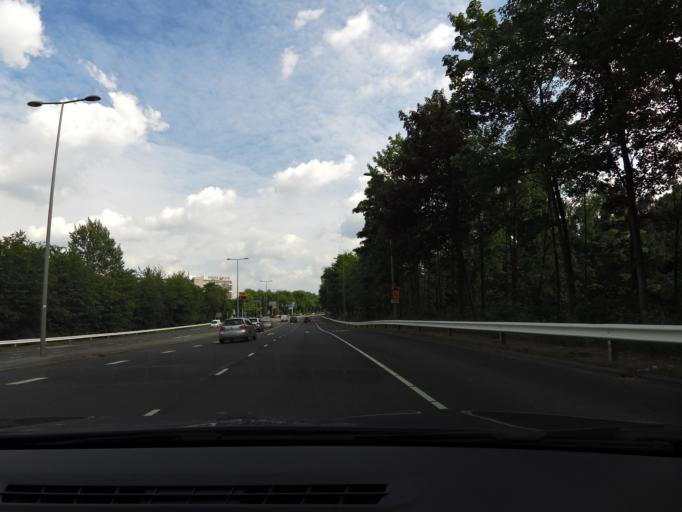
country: NL
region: South Holland
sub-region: Gemeente Barendrecht
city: Barendrecht
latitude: 51.8763
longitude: 4.5085
